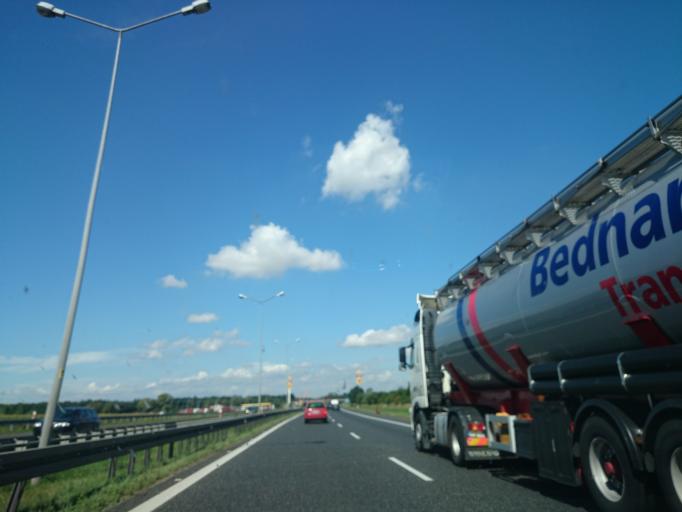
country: PL
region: Lower Silesian Voivodeship
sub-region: Powiat strzelinski
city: Wiazow
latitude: 50.8414
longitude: 17.2623
